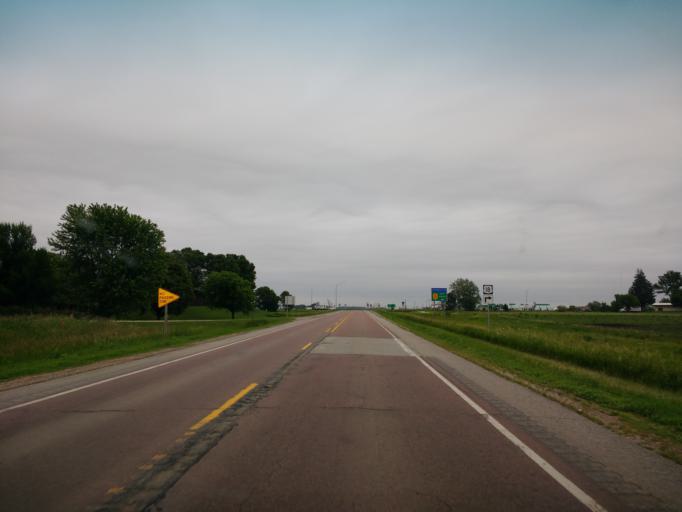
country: US
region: Iowa
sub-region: Clay County
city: Spencer
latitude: 43.1840
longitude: -95.1542
